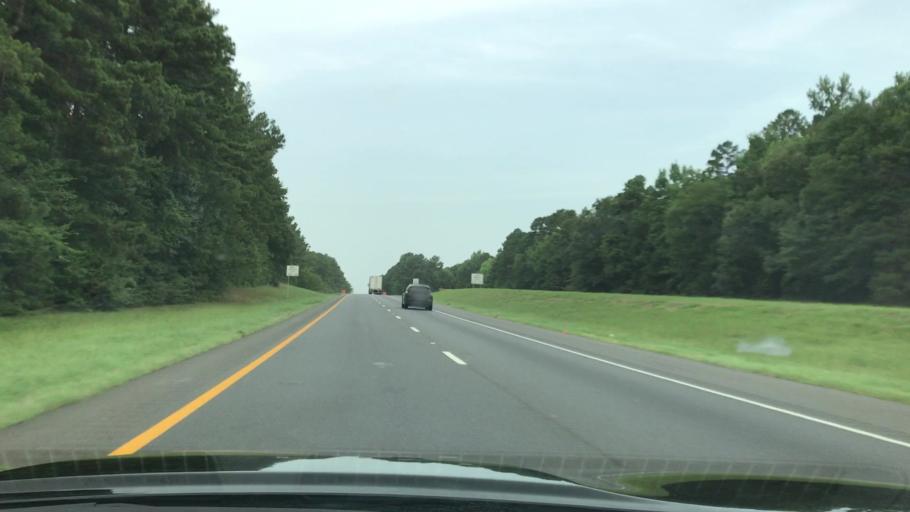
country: US
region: Texas
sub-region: Harrison County
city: Marshall
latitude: 32.4908
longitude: -94.3697
